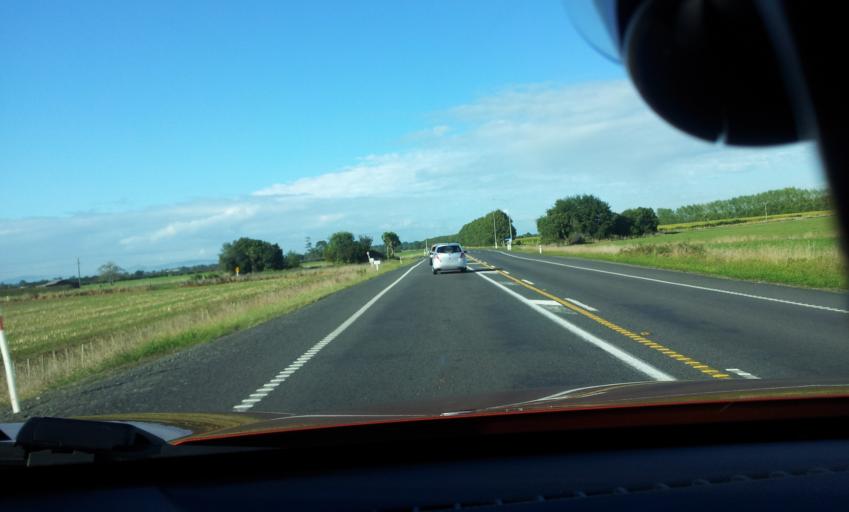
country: NZ
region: Waikato
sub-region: Hauraki District
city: Paeroa
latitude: -37.5271
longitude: 175.5294
